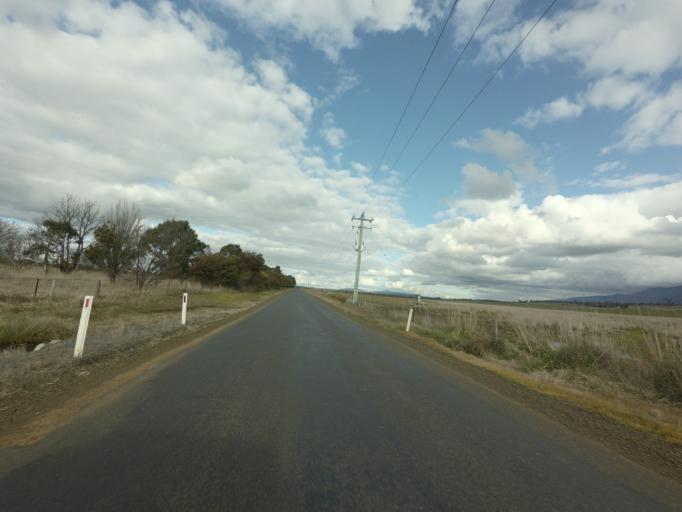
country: AU
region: Tasmania
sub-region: Northern Midlands
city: Longford
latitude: -41.8174
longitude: 147.1969
